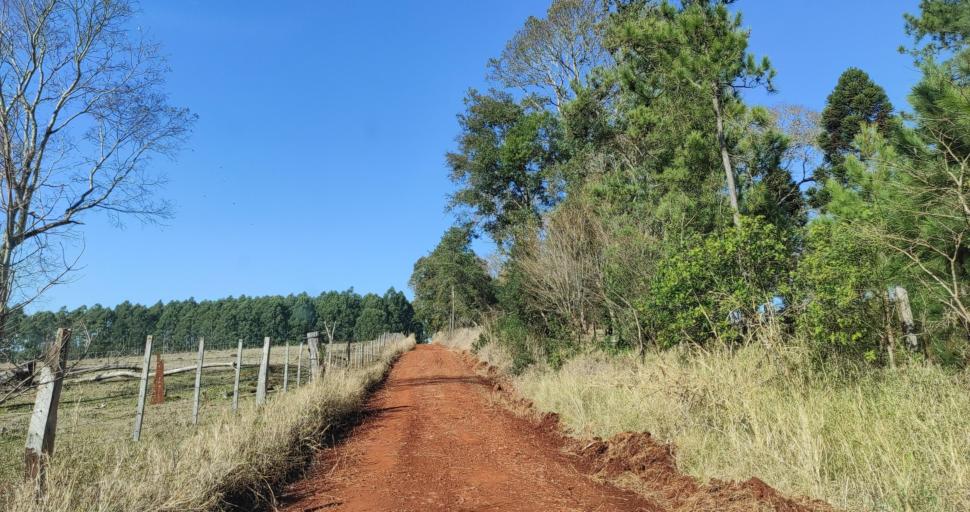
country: AR
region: Misiones
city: Capiovi
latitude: -26.8754
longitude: -55.0365
